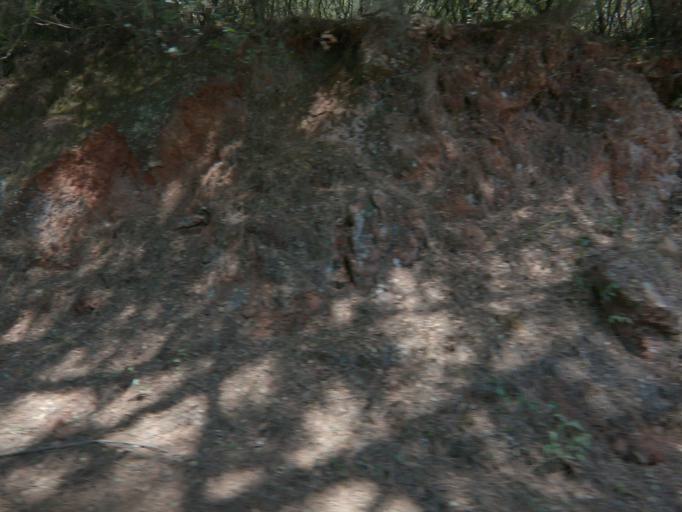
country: PT
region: Setubal
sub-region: Setubal
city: Setubal
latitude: 38.5162
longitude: -8.9305
